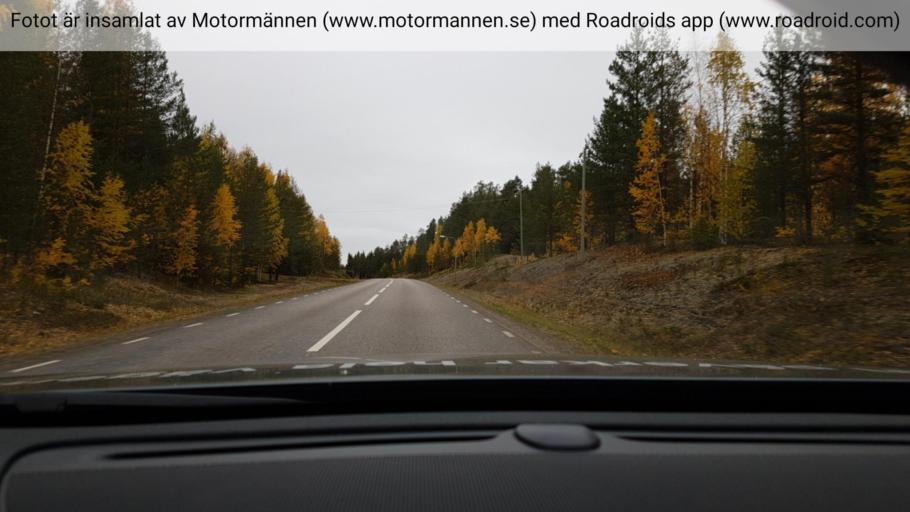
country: SE
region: Norrbotten
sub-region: Overkalix Kommun
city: OEverkalix
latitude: 66.5150
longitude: 22.7673
